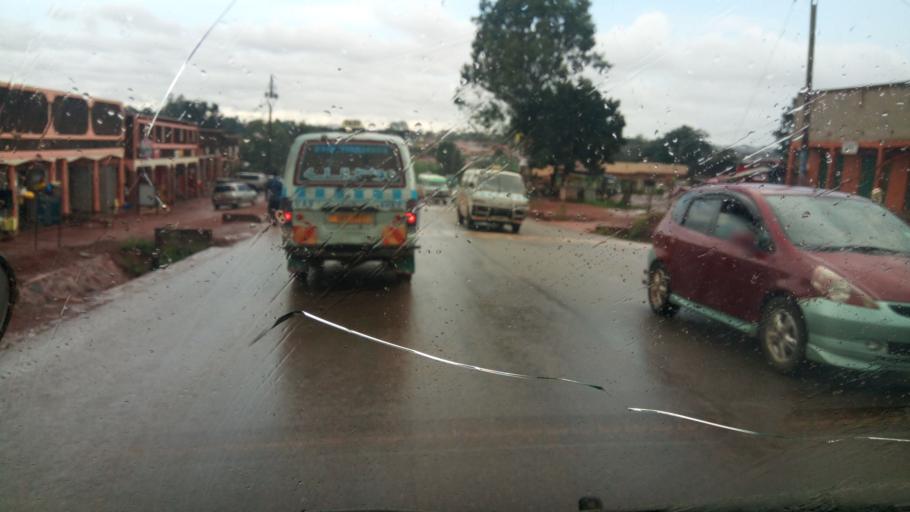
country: UG
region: Central Region
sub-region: Wakiso District
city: Wakiso
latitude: 0.3893
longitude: 32.5091
